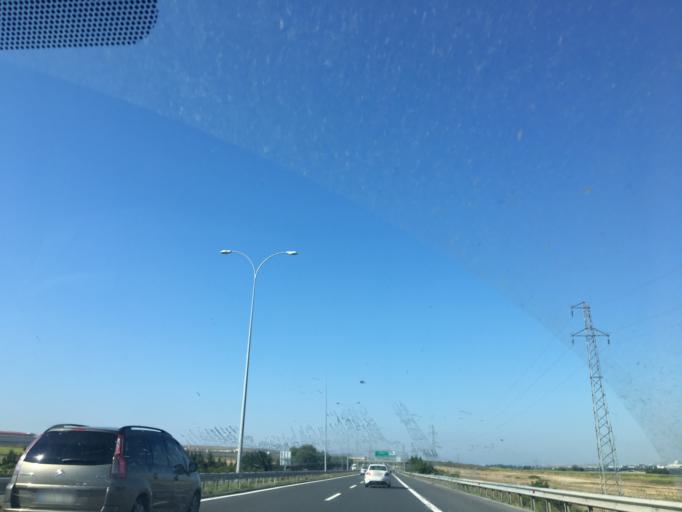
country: TR
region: Istanbul
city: Canta
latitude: 41.1019
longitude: 28.1548
